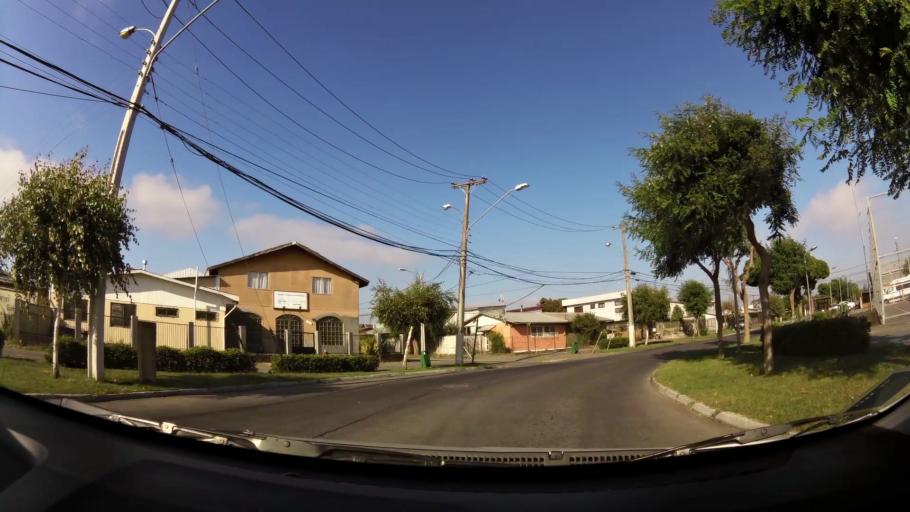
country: CL
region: Biobio
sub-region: Provincia de Concepcion
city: Concepcion
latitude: -36.7918
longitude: -73.1071
